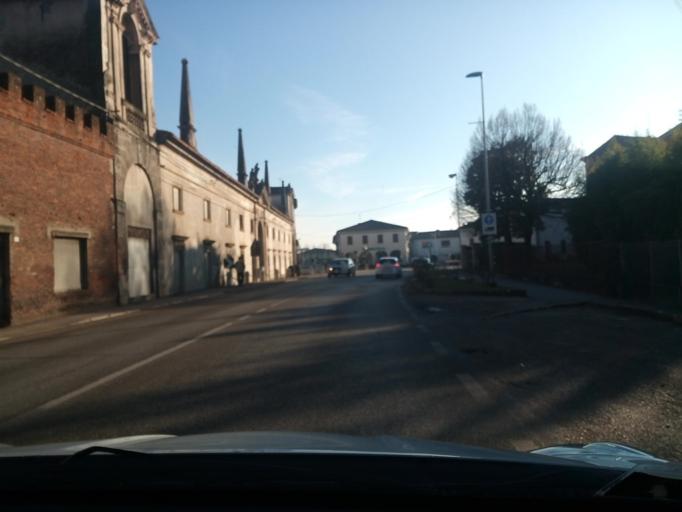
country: IT
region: Veneto
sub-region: Provincia di Vicenza
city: Villaverla
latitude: 45.6524
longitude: 11.4946
